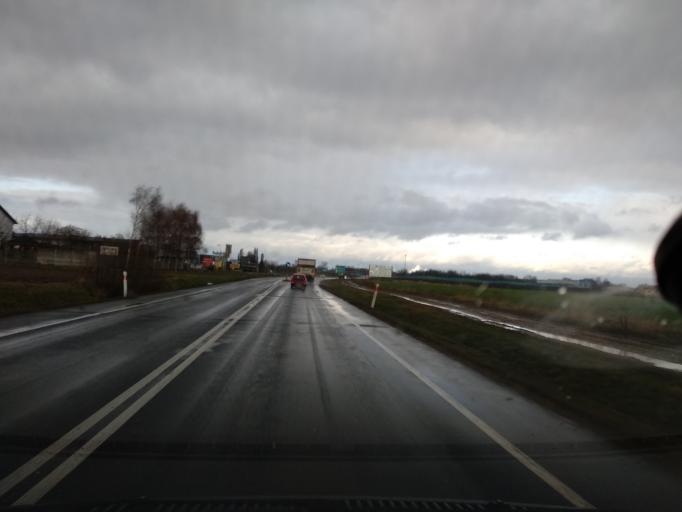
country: PL
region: Greater Poland Voivodeship
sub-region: Powiat koninski
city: Stare Miasto
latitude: 52.1568
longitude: 18.2055
